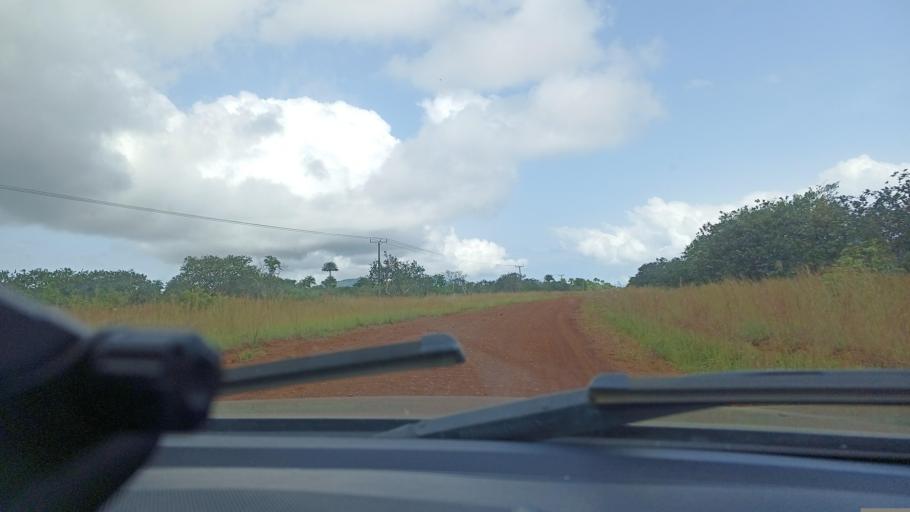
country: LR
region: Grand Cape Mount
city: Robertsport
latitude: 6.6924
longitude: -11.2811
